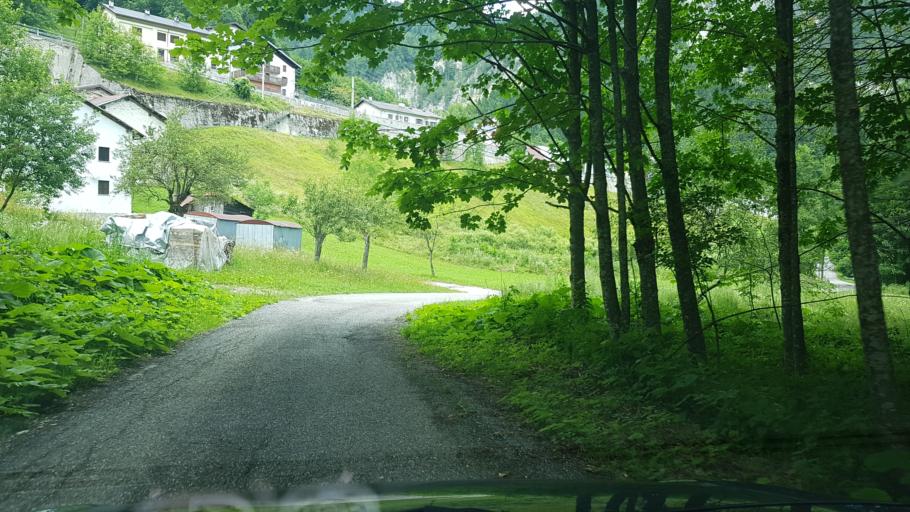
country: IT
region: Friuli Venezia Giulia
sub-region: Provincia di Udine
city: Pontebba
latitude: 46.5031
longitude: 13.2531
